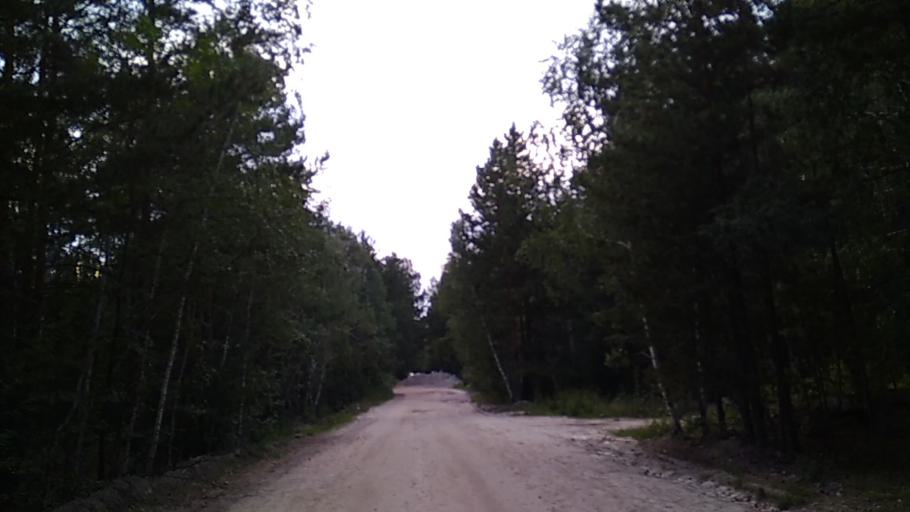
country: RU
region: Chelyabinsk
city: Kyshtym
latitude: 55.6766
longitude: 60.5920
